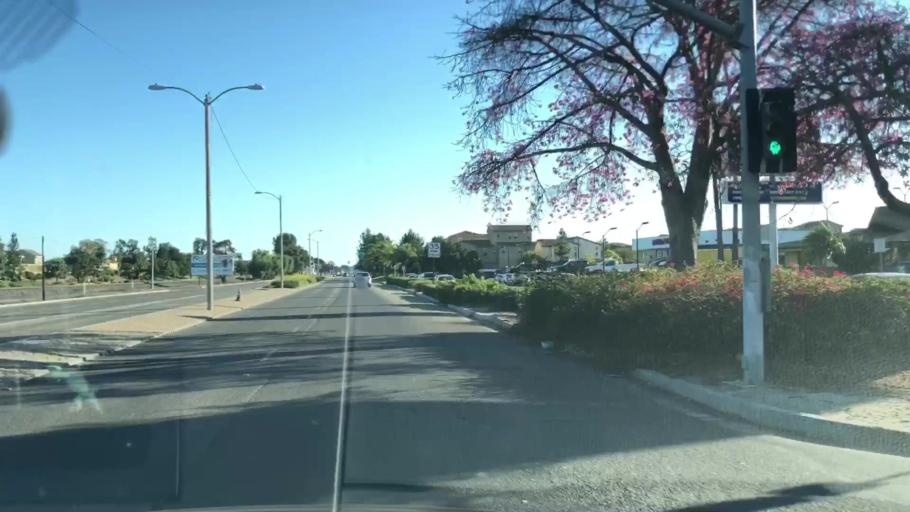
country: US
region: California
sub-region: Ventura County
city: Oxnard
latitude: 34.2143
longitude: -119.1773
